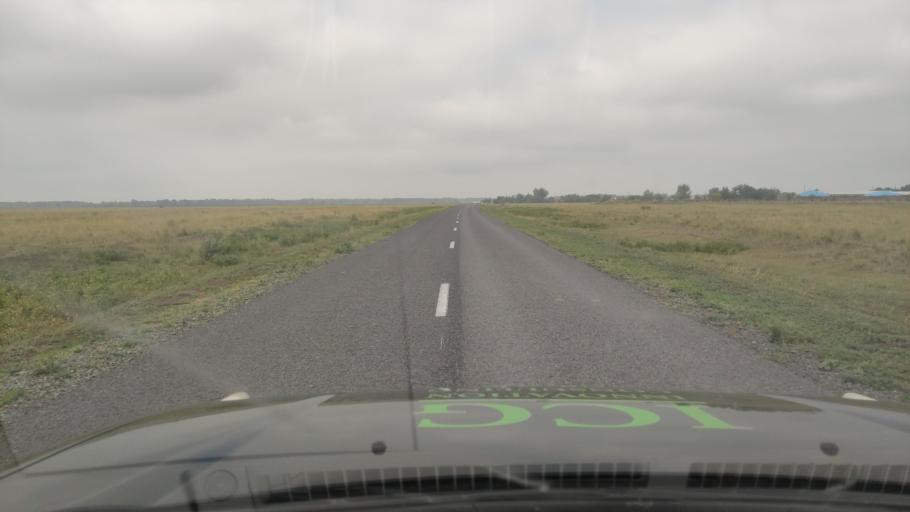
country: KZ
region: Pavlodar
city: Aksu
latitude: 51.9381
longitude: 77.3101
